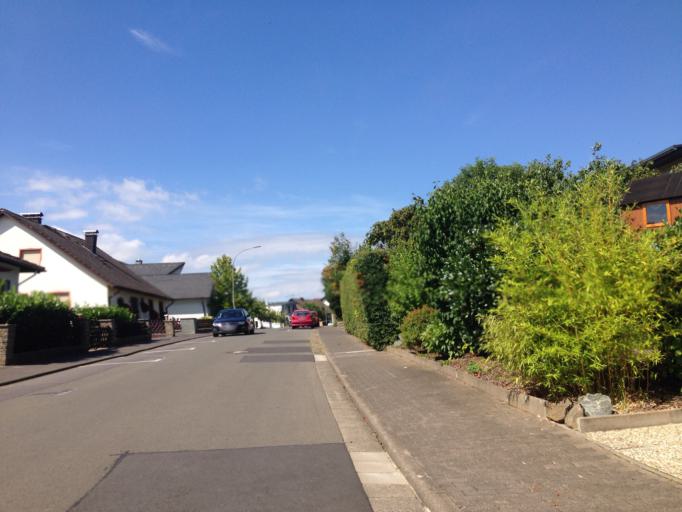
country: DE
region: Hesse
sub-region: Regierungsbezirk Giessen
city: Grunberg
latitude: 50.5919
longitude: 8.9499
